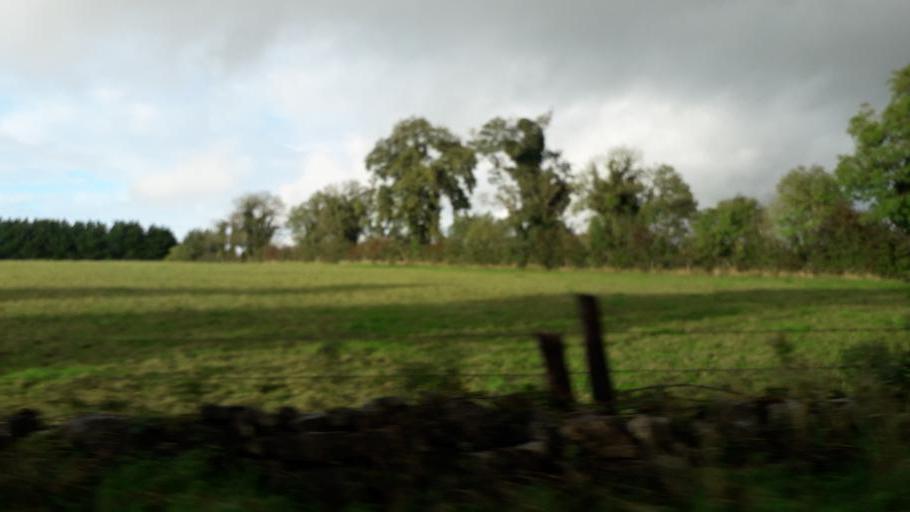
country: IE
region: Leinster
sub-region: An Longfort
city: Lanesborough
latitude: 53.7675
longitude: -8.0981
